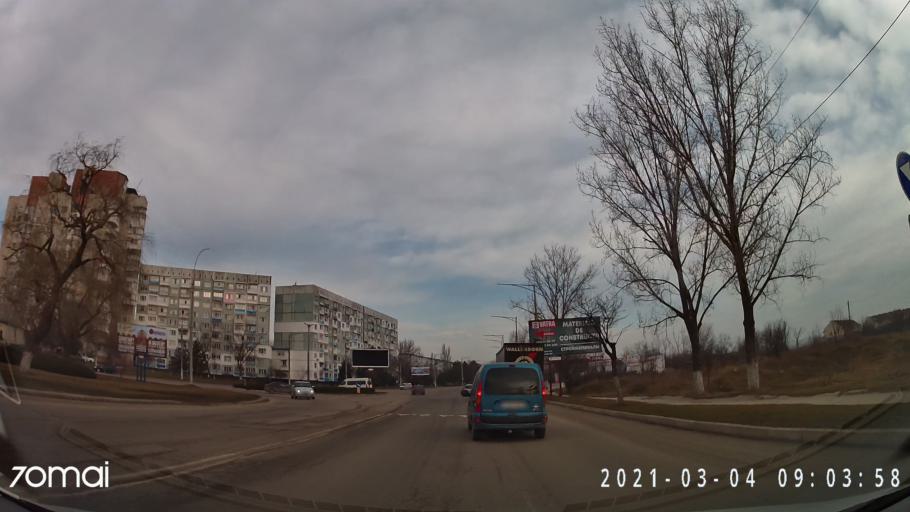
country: MD
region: Balti
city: Balti
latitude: 47.7550
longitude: 27.9419
